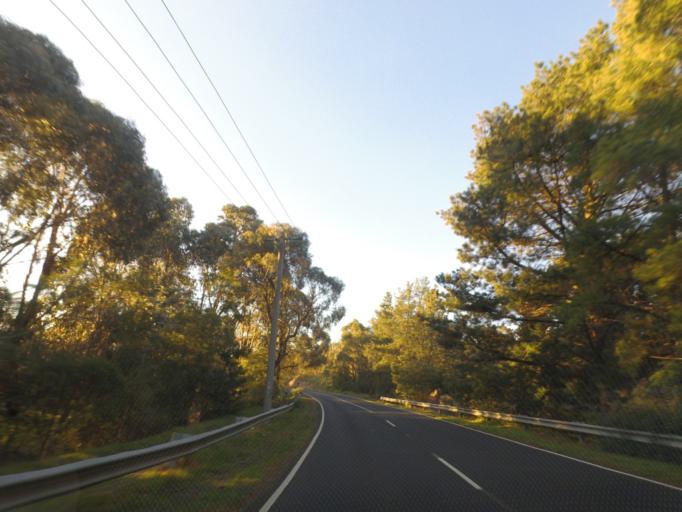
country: AU
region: Victoria
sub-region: Manningham
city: Park Orchards
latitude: -37.7531
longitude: 145.1978
